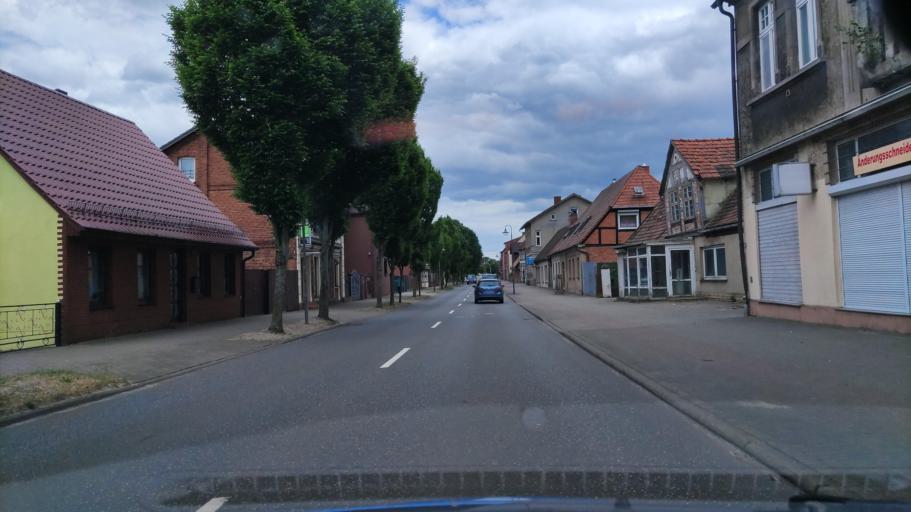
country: DE
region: Mecklenburg-Vorpommern
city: Neustadt-Glewe
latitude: 53.3803
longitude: 11.5897
